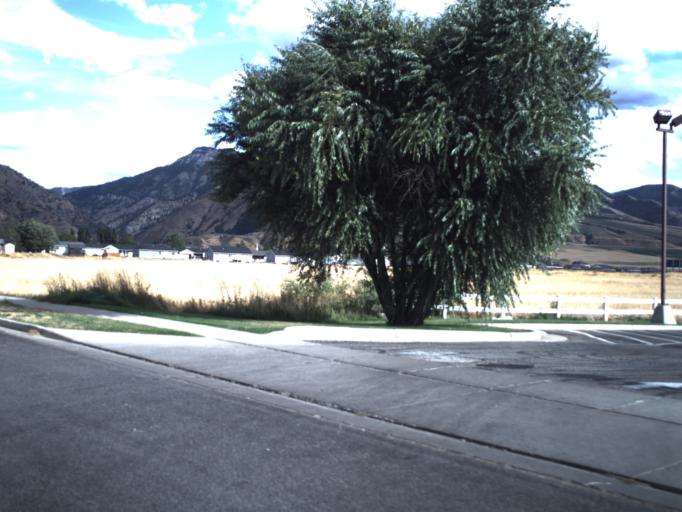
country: US
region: Utah
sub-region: Cache County
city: Hyrum
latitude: 41.6336
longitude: -111.8318
